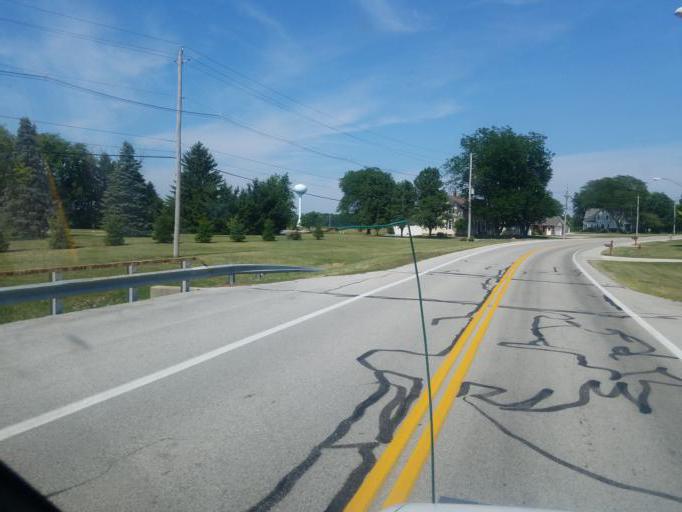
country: US
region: Ohio
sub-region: Auglaize County
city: New Bremen
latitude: 40.4957
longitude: -84.3133
